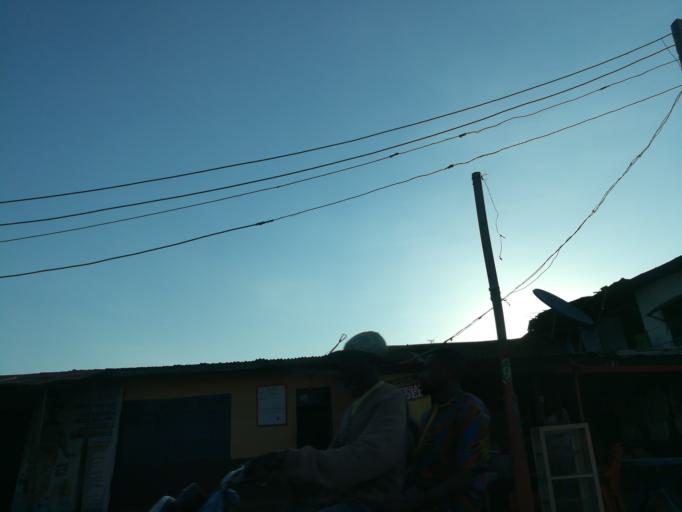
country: NG
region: Lagos
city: Ikorodu
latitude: 6.6155
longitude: 3.5099
